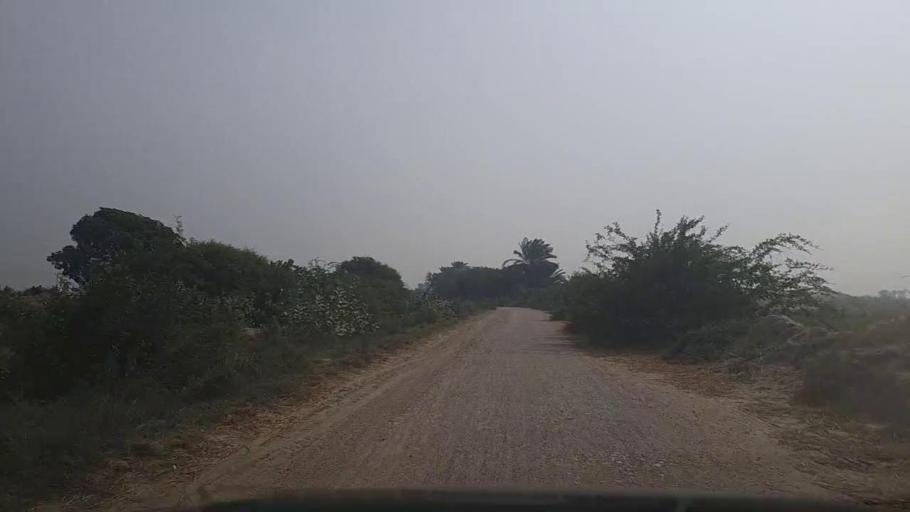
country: PK
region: Sindh
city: Mirpur Sakro
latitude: 24.4810
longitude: 67.6455
